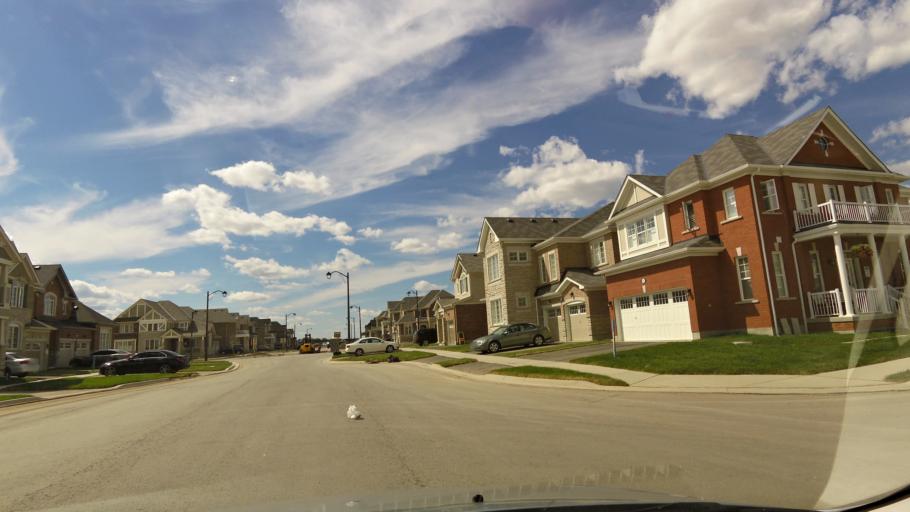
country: CA
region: Ontario
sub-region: Halton
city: Milton
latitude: 43.4858
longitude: -79.8404
